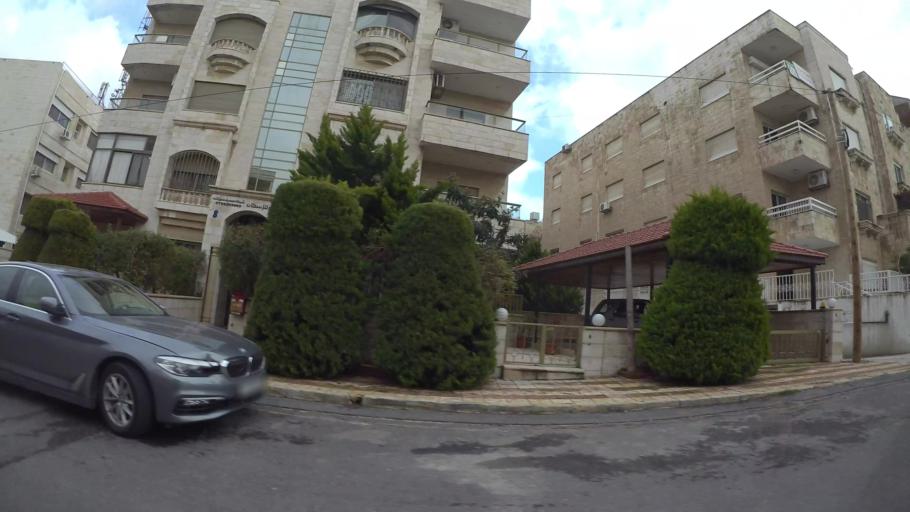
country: JO
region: Amman
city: Al Bunayyat ash Shamaliyah
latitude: 31.9479
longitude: 35.8808
